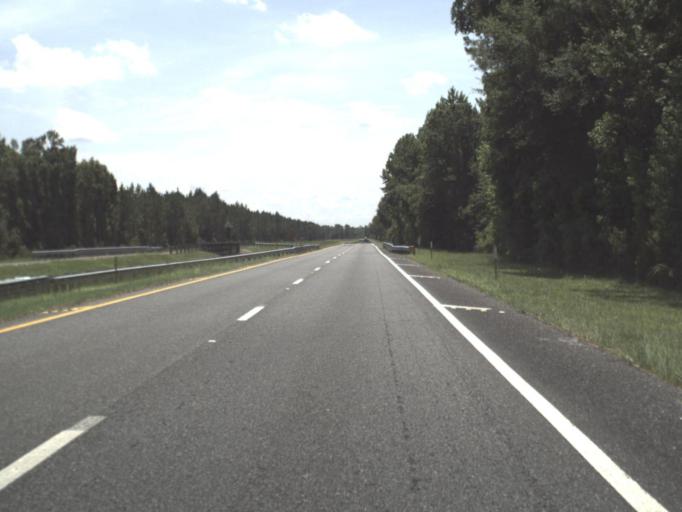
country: US
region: Florida
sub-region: Taylor County
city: Steinhatchee
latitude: 29.7282
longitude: -83.3121
